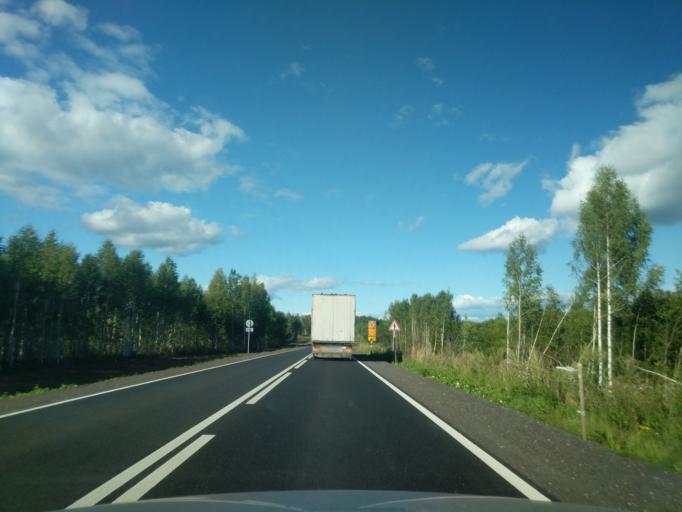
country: RU
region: Kostroma
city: Makar'yev
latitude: 57.9947
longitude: 43.9712
